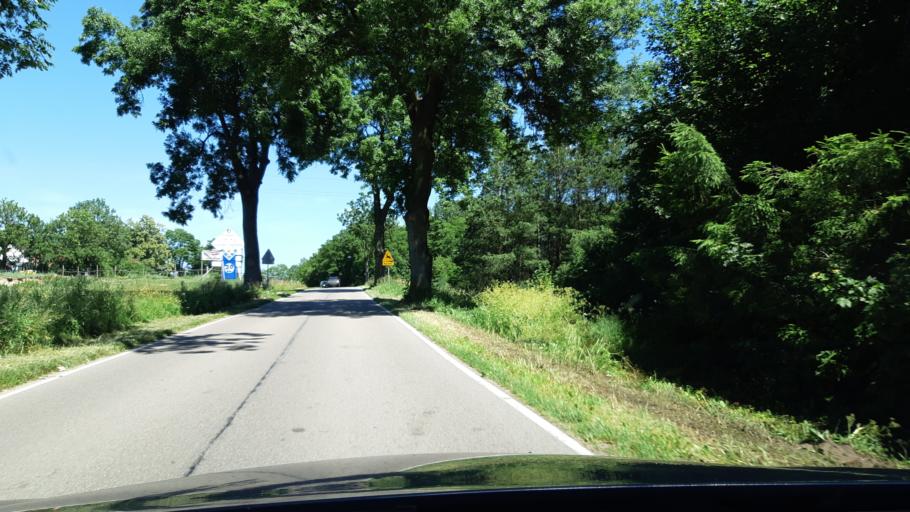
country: PL
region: Warmian-Masurian Voivodeship
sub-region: Powiat gizycki
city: Ryn
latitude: 53.8914
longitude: 21.6596
